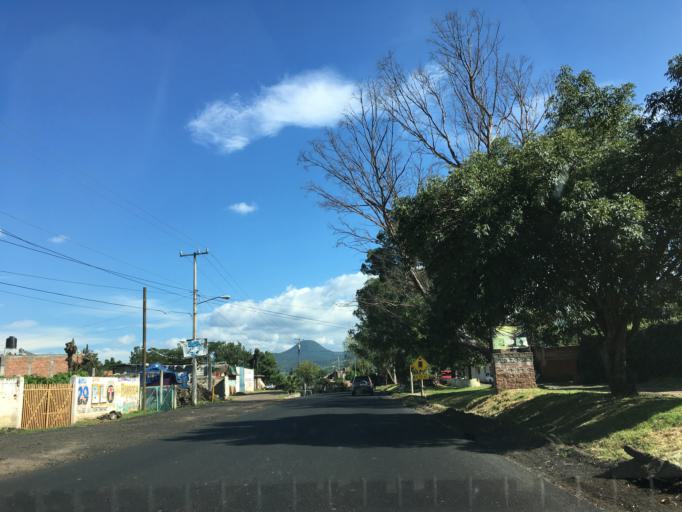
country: MX
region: Michoacan
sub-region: Zacapu
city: Naranja de Tapia
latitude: 19.7811
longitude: -101.7659
